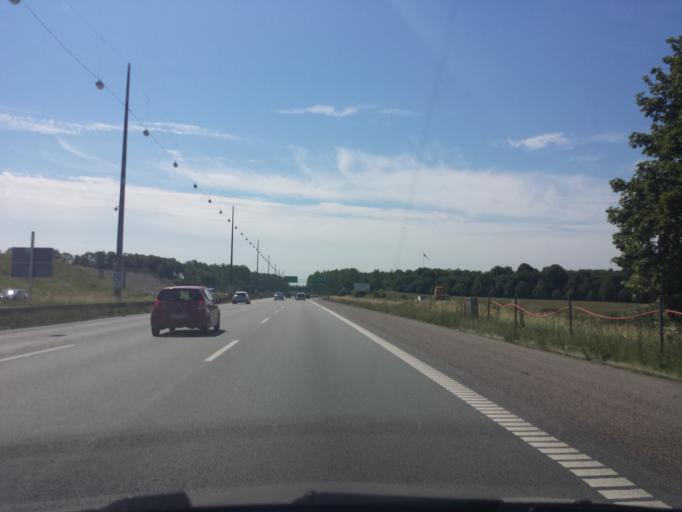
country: DK
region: Capital Region
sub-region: Brondby Kommune
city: Brondbyvester
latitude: 55.6451
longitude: 12.4343
